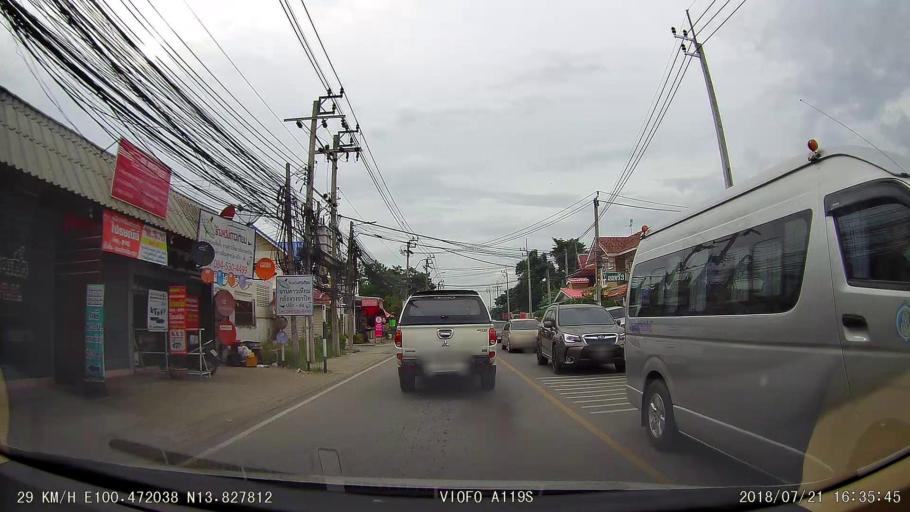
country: TH
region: Nonthaburi
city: Bang Kruai
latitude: 13.8278
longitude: 100.4720
